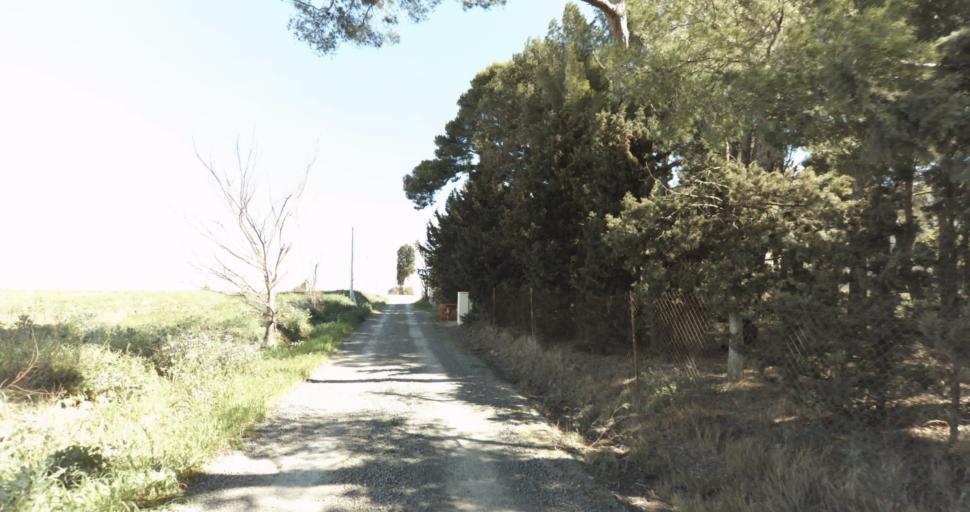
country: FR
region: Languedoc-Roussillon
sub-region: Departement de l'Herault
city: Marseillan
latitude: 43.3859
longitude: 3.5436
